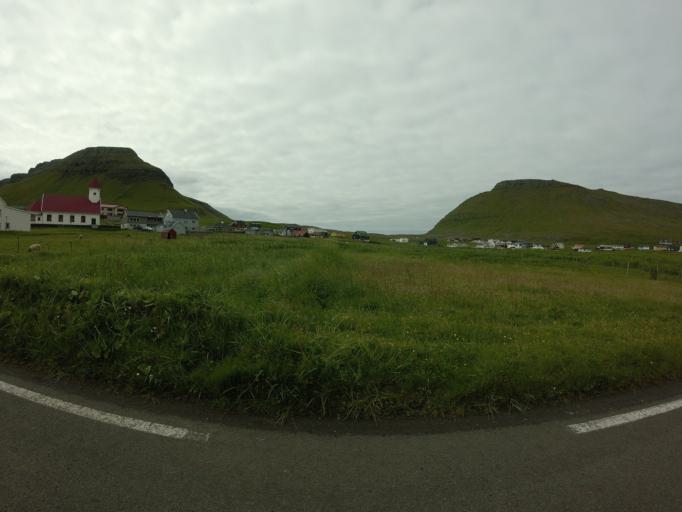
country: FO
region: Suduroy
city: Tvoroyri
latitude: 61.5988
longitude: -6.9530
